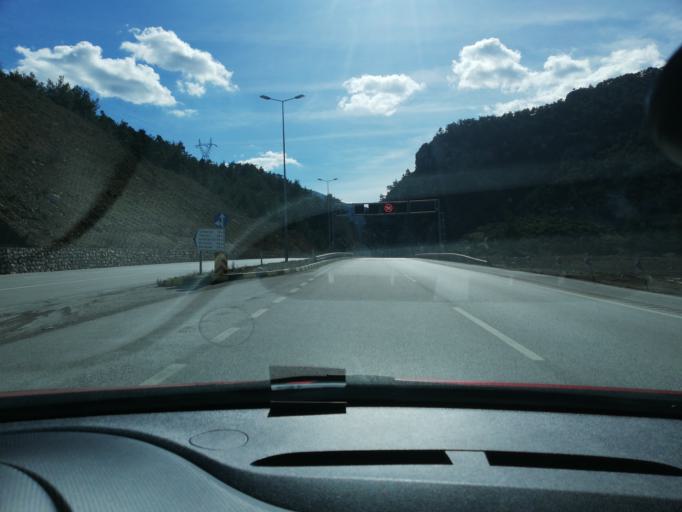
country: TR
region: Karabuk
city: Karabuk
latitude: 41.0850
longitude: 32.6747
